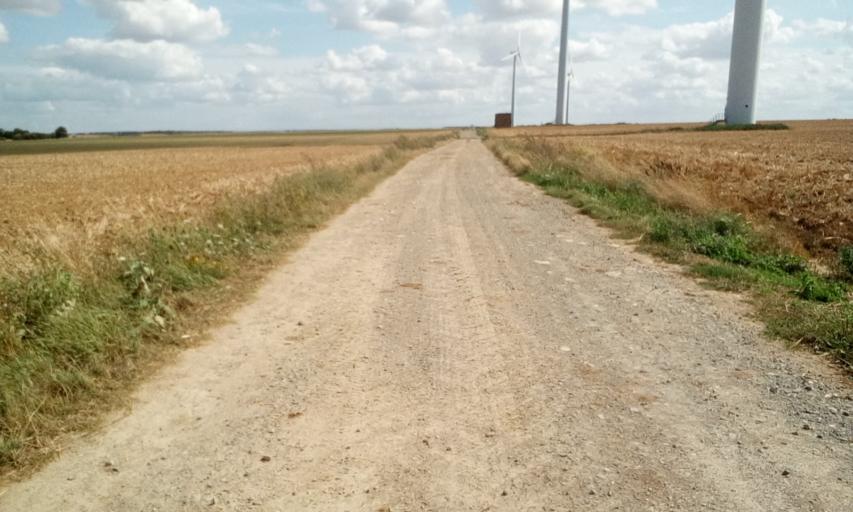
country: FR
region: Lower Normandy
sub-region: Departement du Calvados
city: Bellengreville
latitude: 49.1013
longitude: -0.2314
